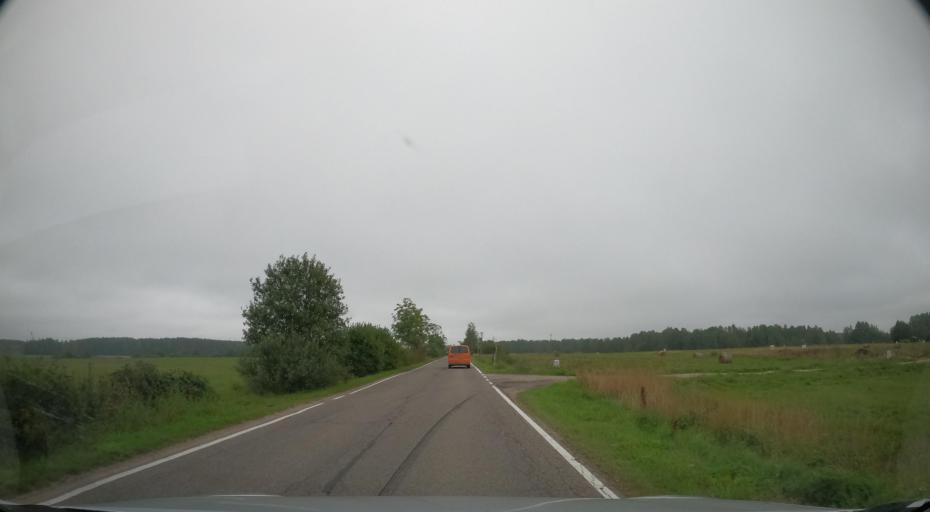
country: PL
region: Pomeranian Voivodeship
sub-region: Powiat wejherowski
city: Szemud
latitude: 54.5023
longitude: 18.1603
